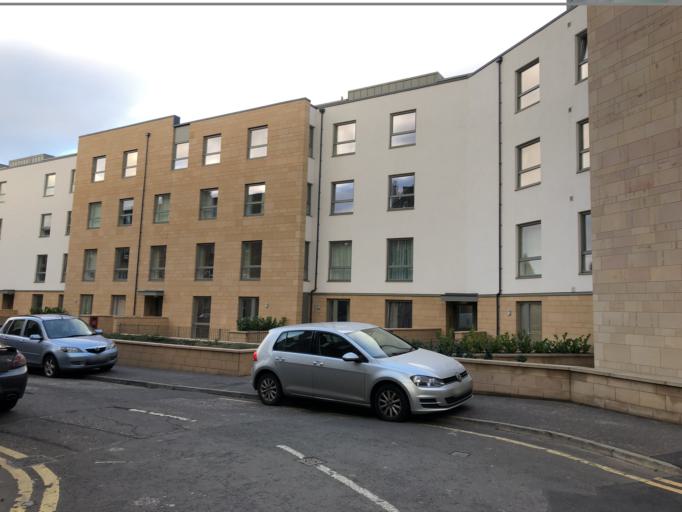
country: GB
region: Scotland
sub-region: West Lothian
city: Seafield
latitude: 55.9579
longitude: -3.1597
